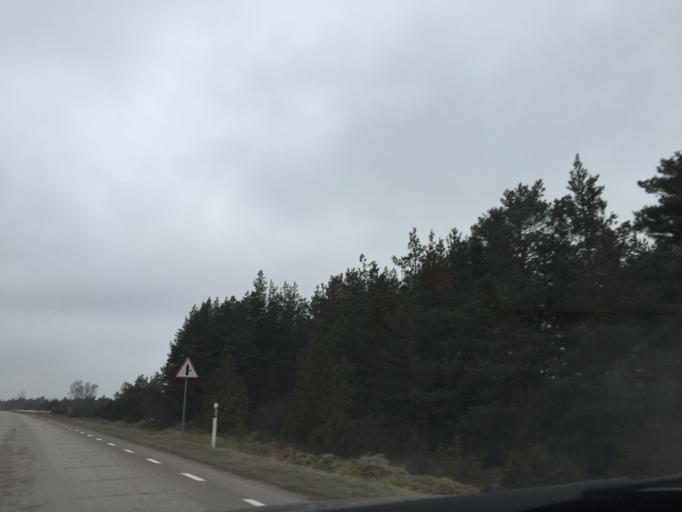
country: EE
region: Saare
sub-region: Kuressaare linn
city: Kuressaare
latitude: 58.2879
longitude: 22.4068
